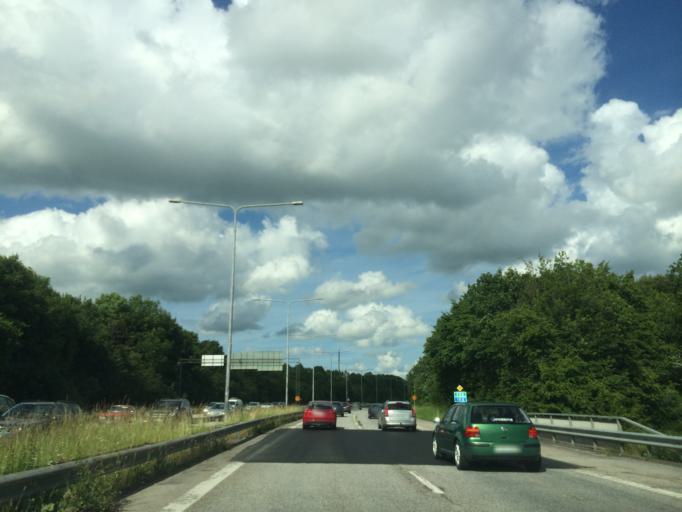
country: SE
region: Skane
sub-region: Lunds Kommun
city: Lund
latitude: 55.7176
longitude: 13.1676
